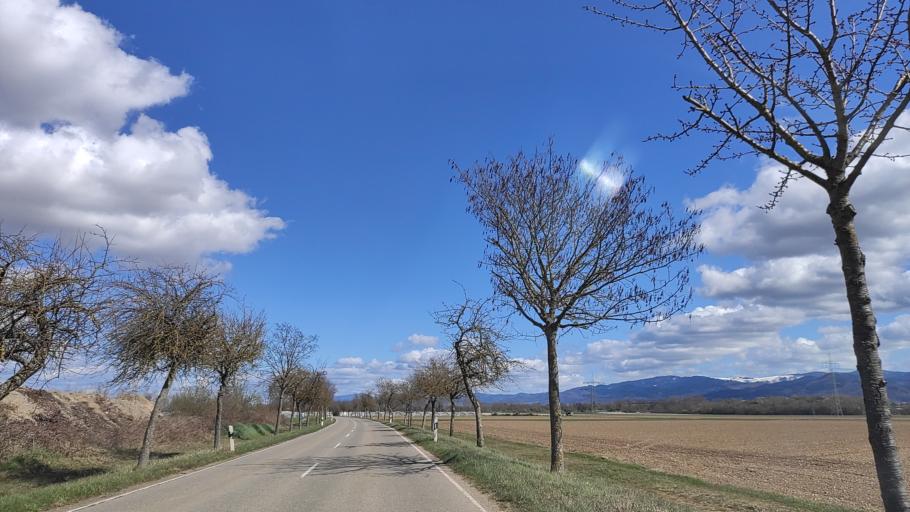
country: DE
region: Baden-Wuerttemberg
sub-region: Freiburg Region
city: Heitersheim
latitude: 47.8791
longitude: 7.6222
